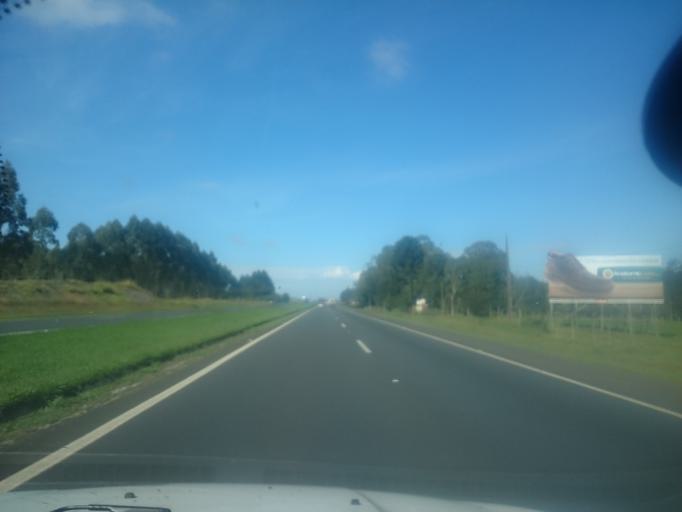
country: BR
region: Parana
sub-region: Palmeira
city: Palmeira
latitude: -25.4205
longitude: -49.7675
